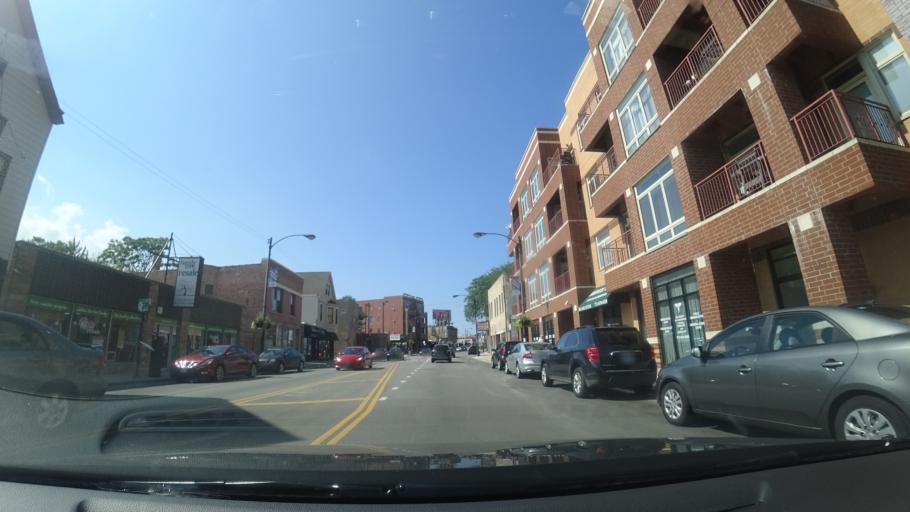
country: US
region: Illinois
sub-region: Cook County
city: Lincolnwood
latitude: 41.9733
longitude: -87.6916
